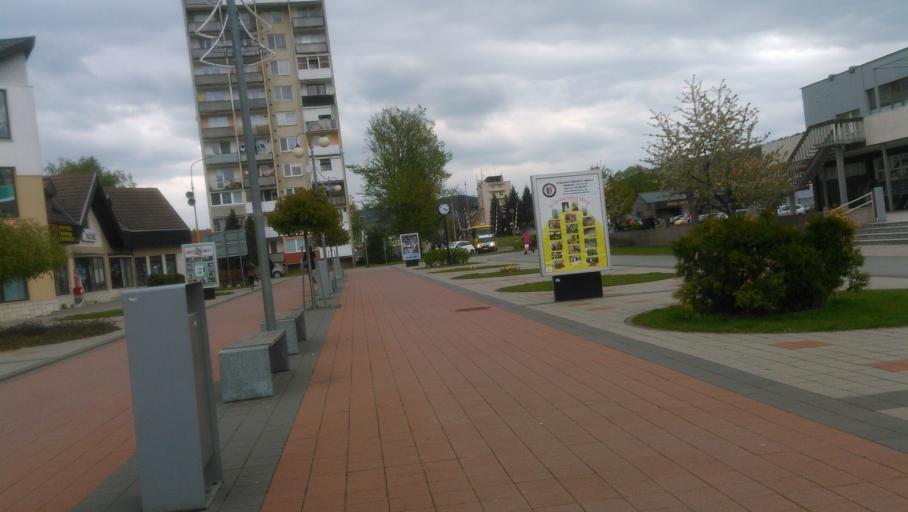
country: SK
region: Presovsky
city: Humenne
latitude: 48.9315
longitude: 21.9121
